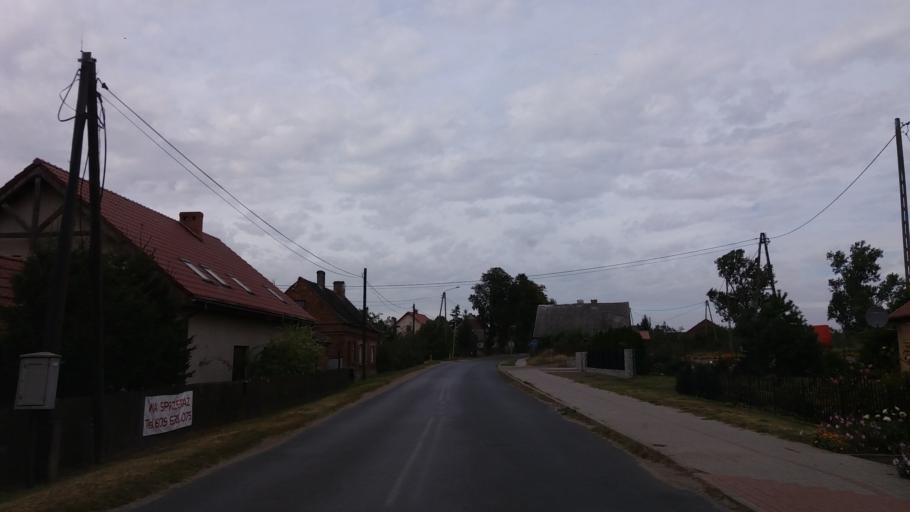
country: PL
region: Lubusz
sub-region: Powiat strzelecko-drezdenecki
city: Strzelce Krajenskie
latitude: 52.9024
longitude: 15.5045
